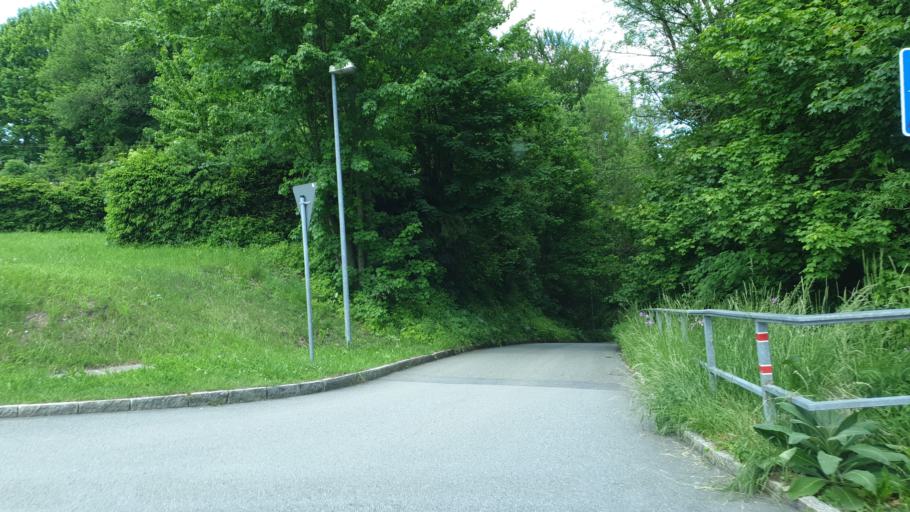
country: DE
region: Saxony
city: Schwarzenberg
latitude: 50.5456
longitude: 12.7701
